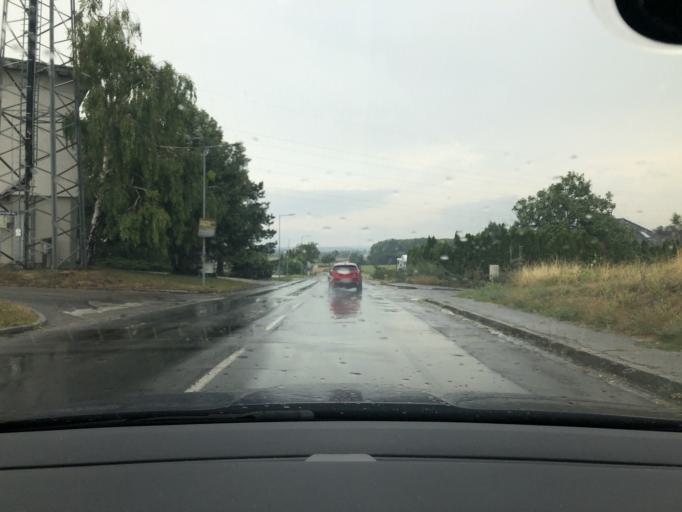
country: AT
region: Lower Austria
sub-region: Politischer Bezirk Ganserndorf
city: Ganserndorf
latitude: 48.3440
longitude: 16.7143
